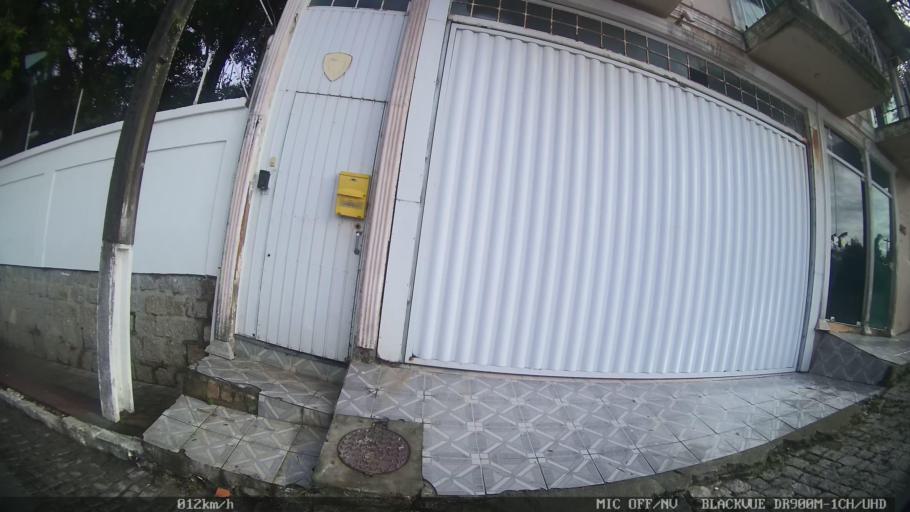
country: BR
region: Santa Catarina
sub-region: Sao Jose
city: Campinas
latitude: -27.6149
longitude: -48.6274
